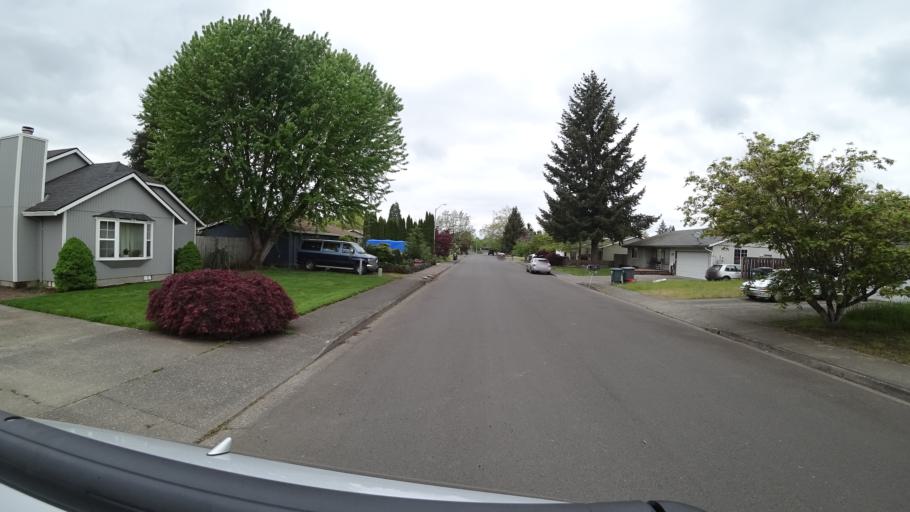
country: US
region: Oregon
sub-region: Washington County
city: Hillsboro
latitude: 45.5381
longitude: -122.9756
